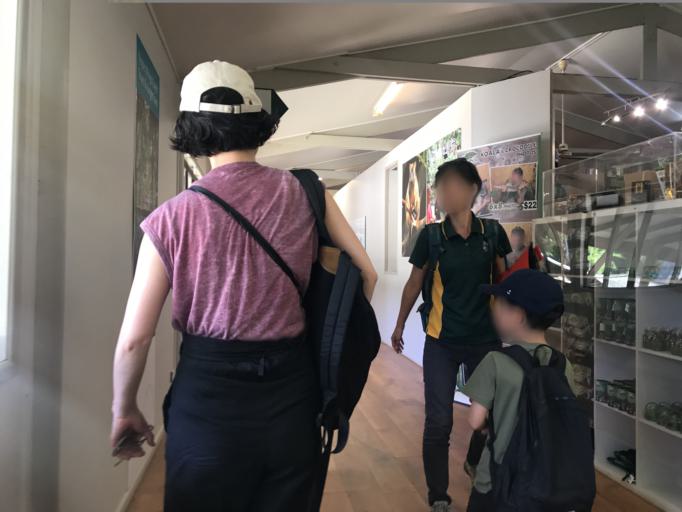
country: AU
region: Queensland
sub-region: Tablelands
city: Kuranda
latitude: -16.8238
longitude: 145.6519
